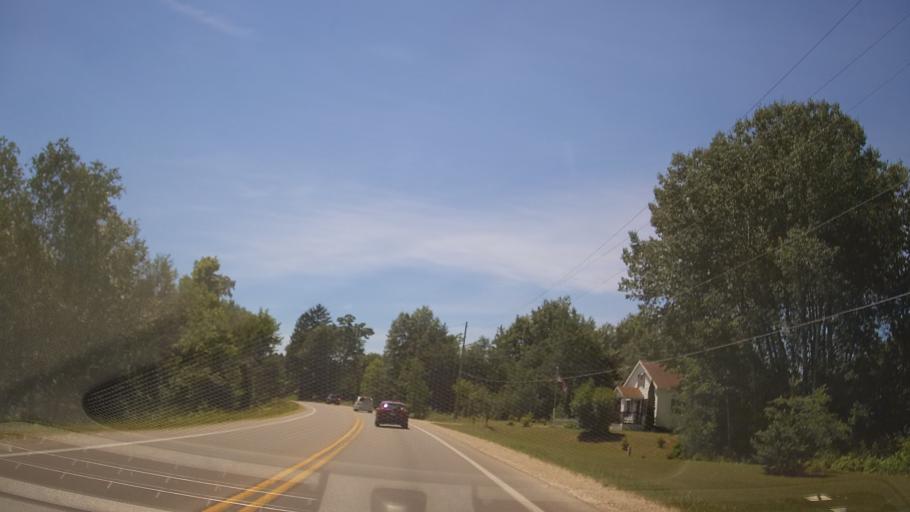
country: US
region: Michigan
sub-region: Grand Traverse County
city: Traverse City
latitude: 44.7324
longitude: -85.6597
